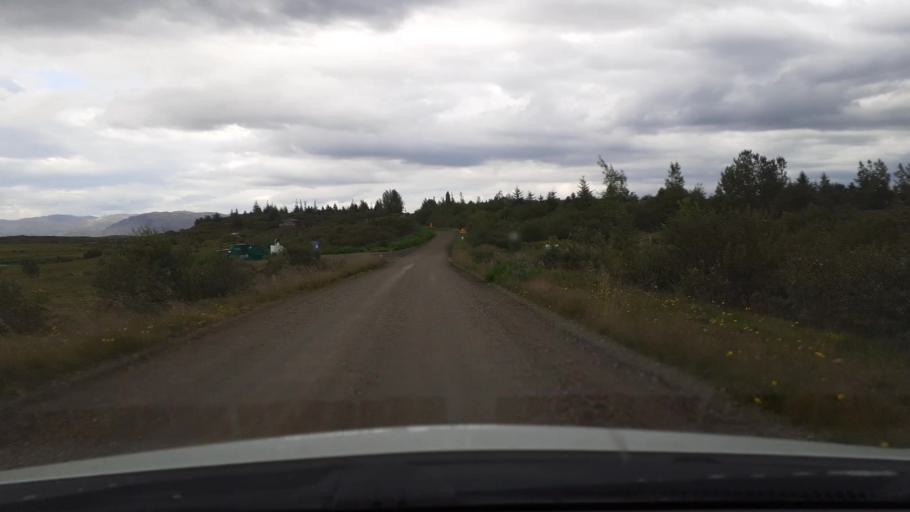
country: IS
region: West
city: Borgarnes
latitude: 64.6131
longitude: -21.9512
